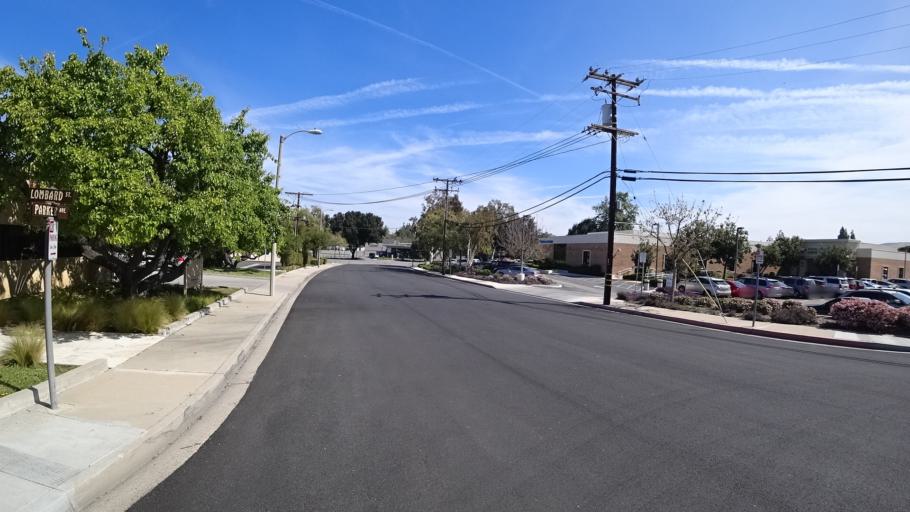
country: US
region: California
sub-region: Ventura County
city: Thousand Oaks
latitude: 34.1782
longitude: -118.8721
